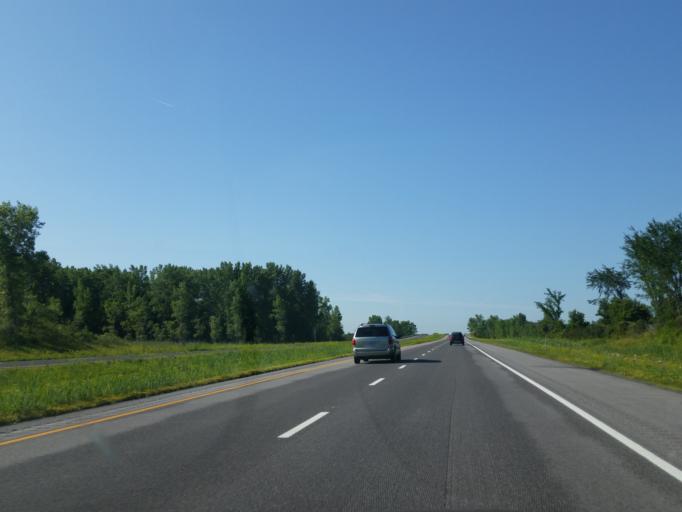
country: CA
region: Quebec
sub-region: Monteregie
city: Napierville
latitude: 45.2444
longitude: -73.4731
